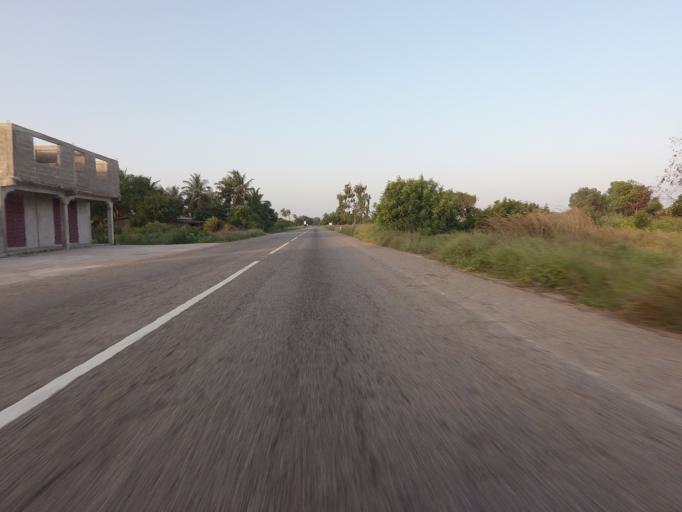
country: GH
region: Volta
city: Anloga
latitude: 5.7866
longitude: 0.8557
